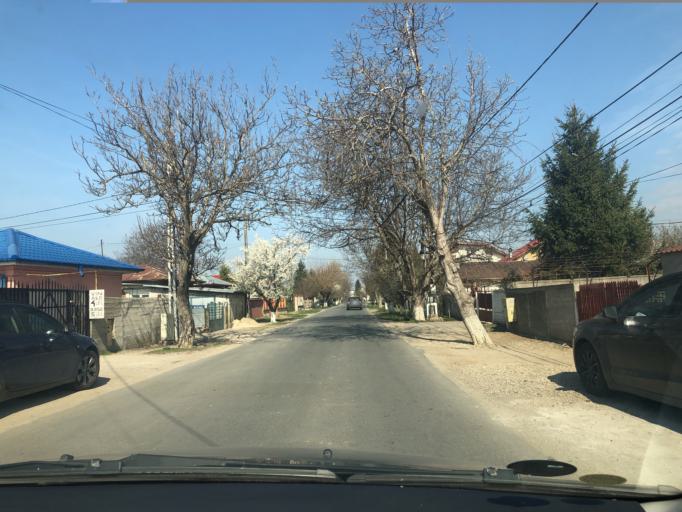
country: RO
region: Ilfov
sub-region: Comuna Clinceni
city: Clinceni
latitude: 44.3744
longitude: 25.9545
